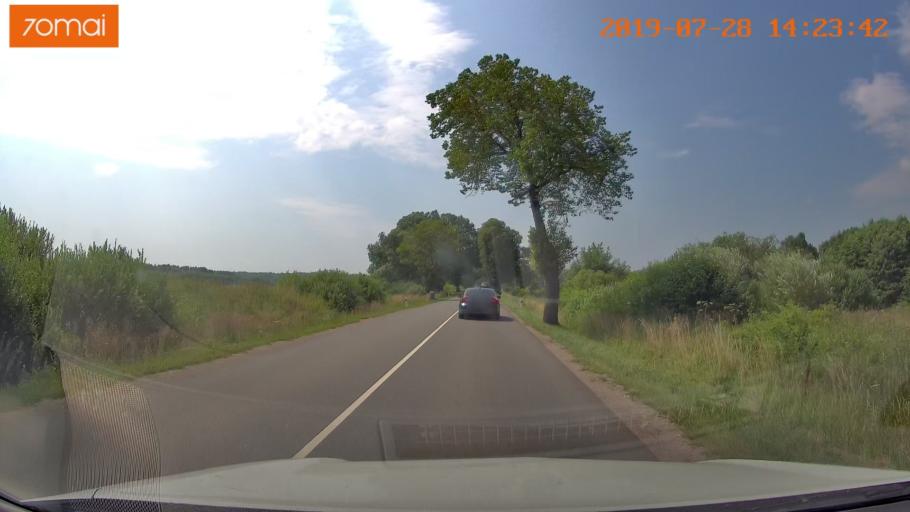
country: RU
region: Kaliningrad
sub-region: Gorod Svetlogorsk
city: Svetlogorsk
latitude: 54.8146
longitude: 20.1625
